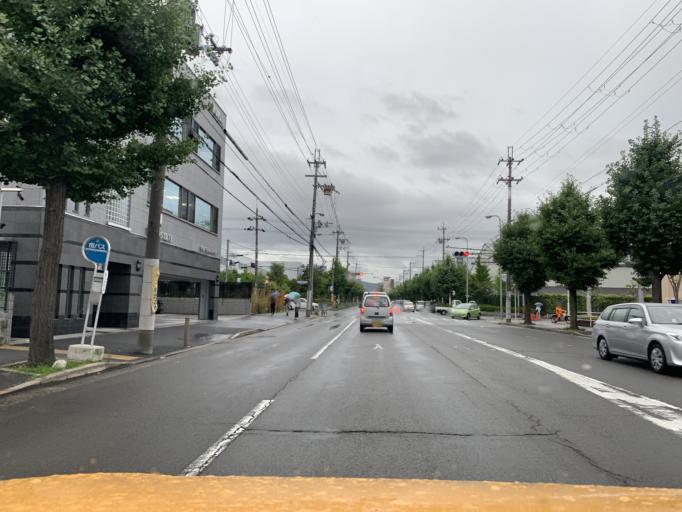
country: JP
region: Kyoto
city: Kyoto
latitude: 35.0109
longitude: 135.7248
